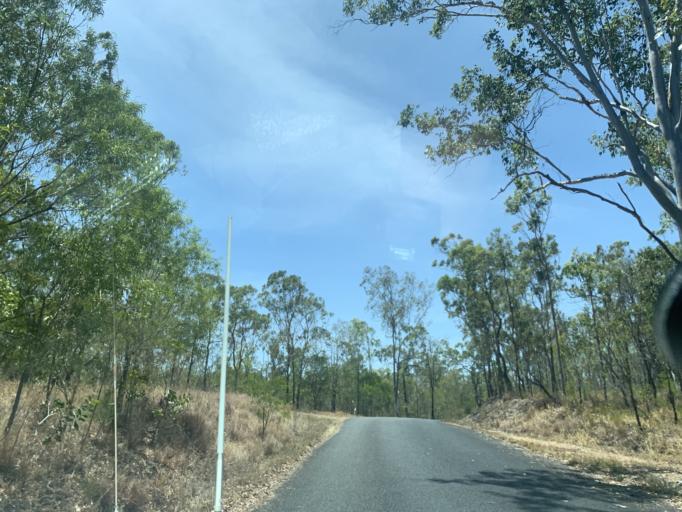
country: AU
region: Queensland
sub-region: Tablelands
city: Kuranda
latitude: -16.9188
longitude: 145.5822
